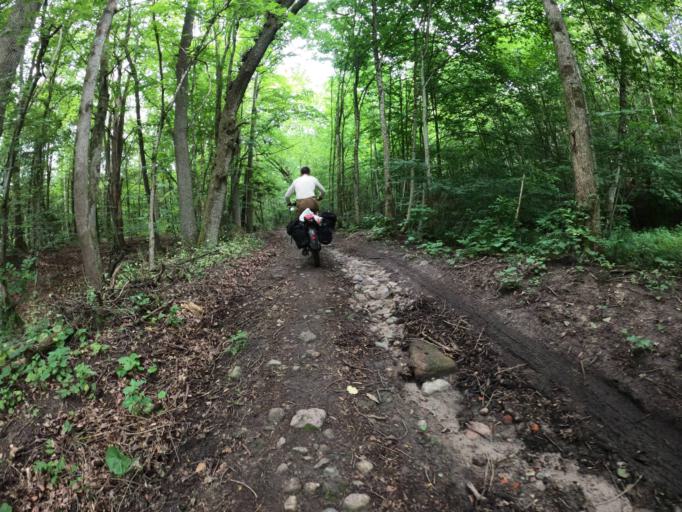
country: PL
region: West Pomeranian Voivodeship
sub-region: Powiat bialogardzki
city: Tychowo
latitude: 53.9773
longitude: 16.3945
